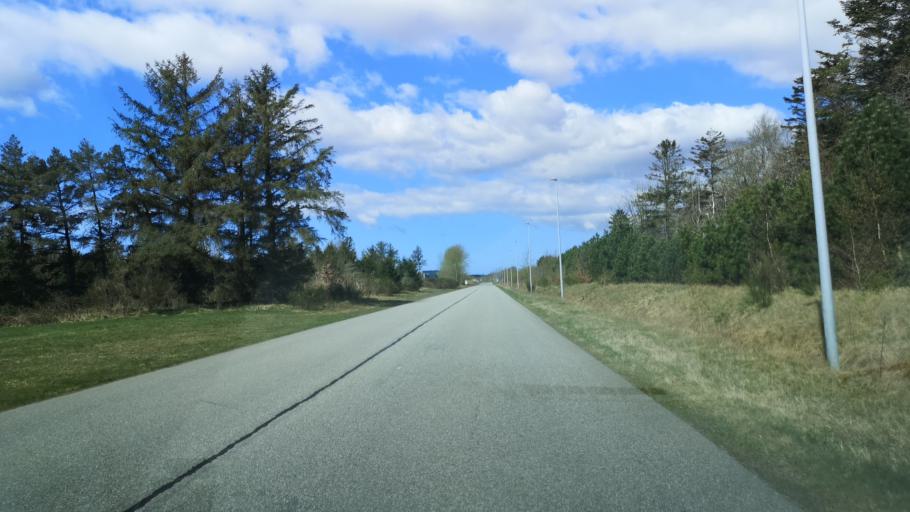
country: DK
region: Central Jutland
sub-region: Ringkobing-Skjern Kommune
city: Skjern
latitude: 55.9624
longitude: 8.5067
